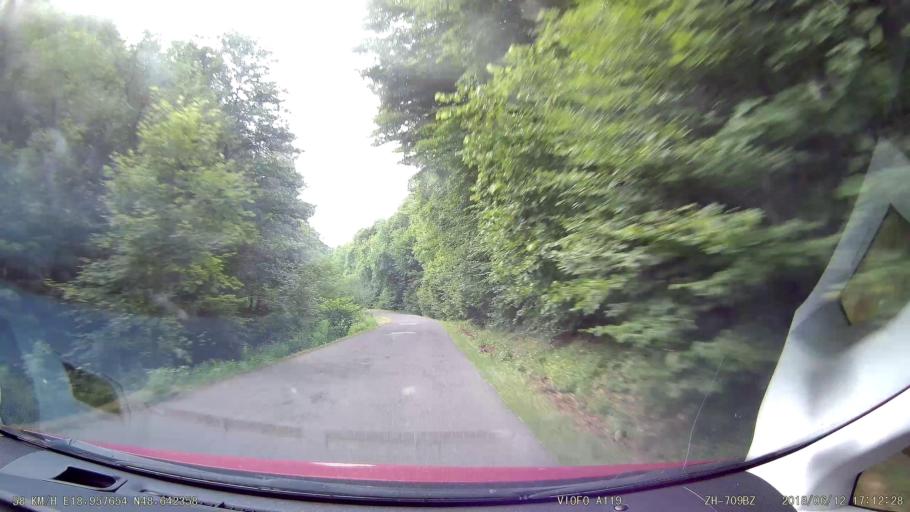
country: SK
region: Banskobystricky
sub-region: Okres Ziar nad Hronom
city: Kremnica
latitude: 48.6425
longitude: 18.9576
